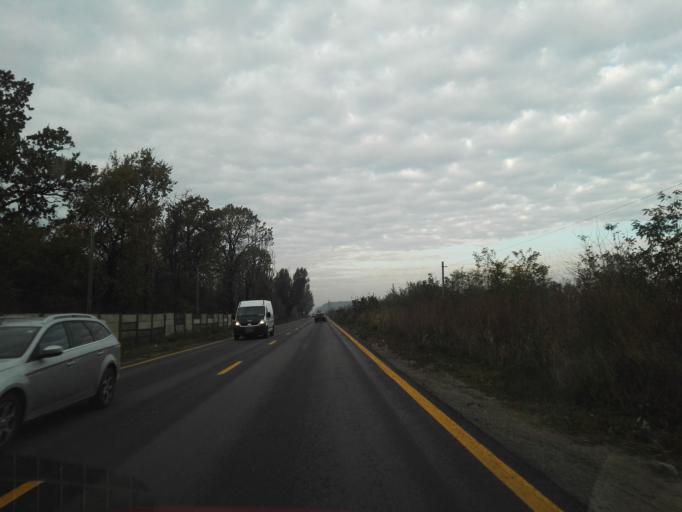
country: RO
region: Ilfov
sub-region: Comuna Magurele
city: Alunisu
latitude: 44.3480
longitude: 26.0709
